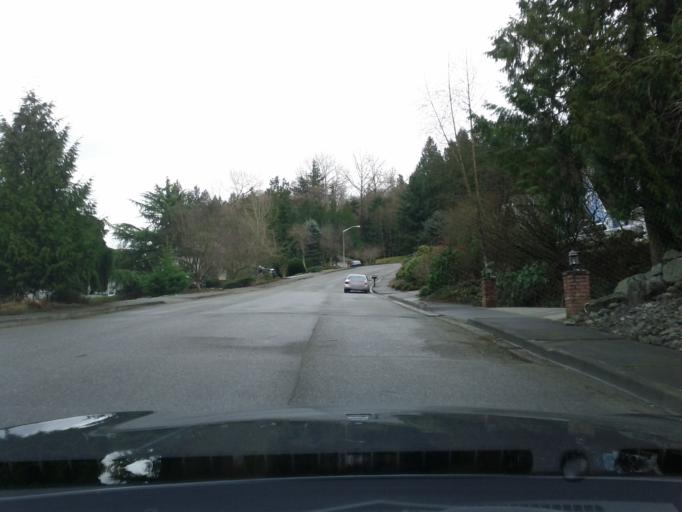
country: US
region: Washington
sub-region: Skagit County
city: Big Lake
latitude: 48.4314
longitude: -122.2838
